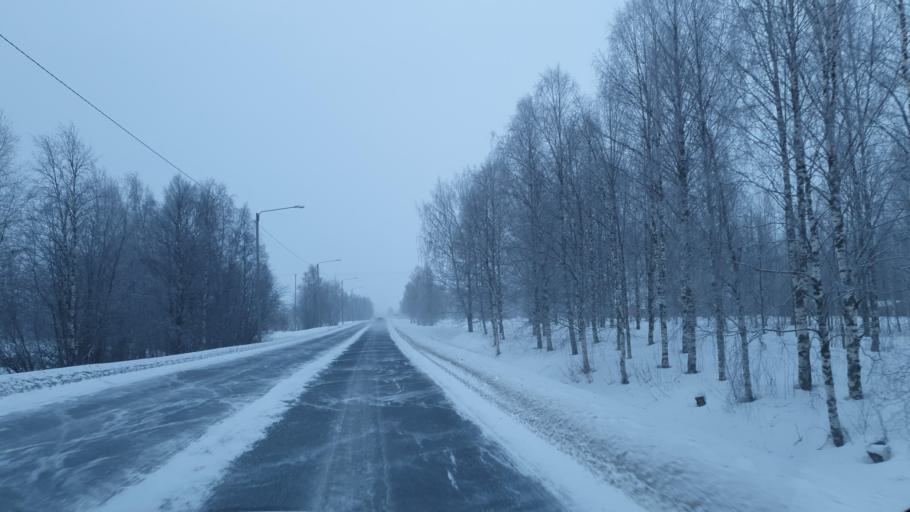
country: FI
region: Lapland
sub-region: Kemi-Tornio
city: Tornio
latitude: 65.9253
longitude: 24.1305
